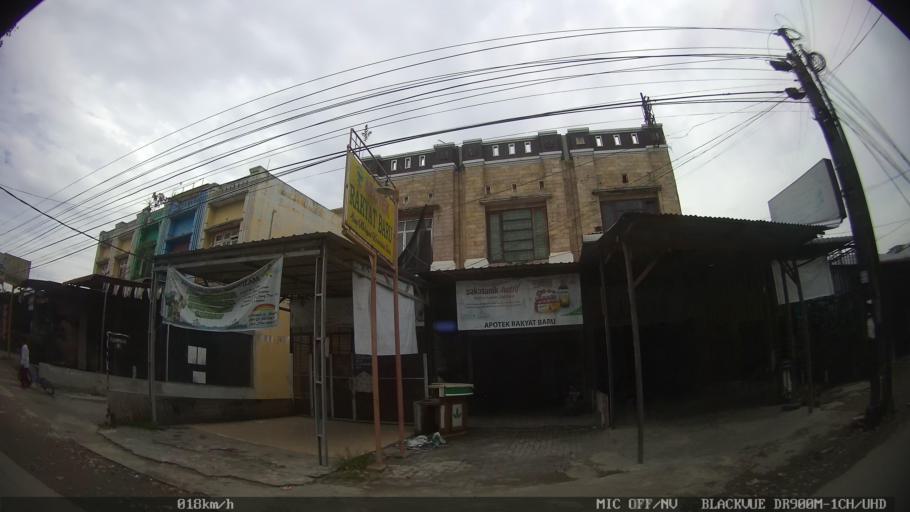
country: ID
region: North Sumatra
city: Sunggal
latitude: 3.6131
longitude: 98.6054
